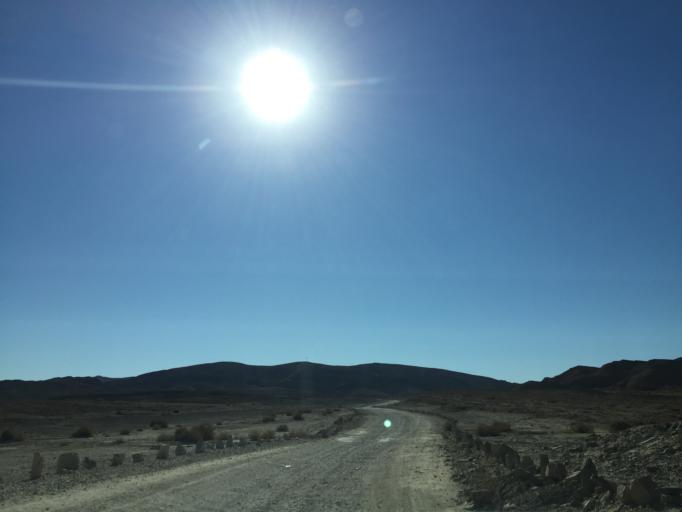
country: IL
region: Southern District
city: Mitzpe Ramon
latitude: 30.6019
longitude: 34.8960
